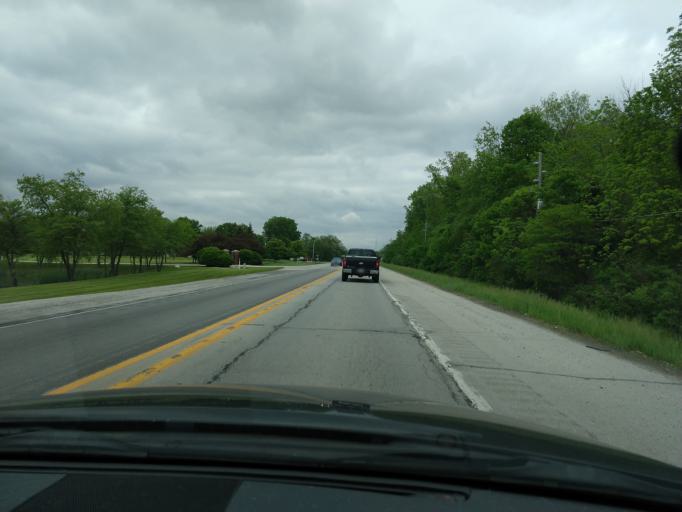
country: US
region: Indiana
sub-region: Hamilton County
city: Westfield
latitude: 40.0429
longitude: -86.1022
